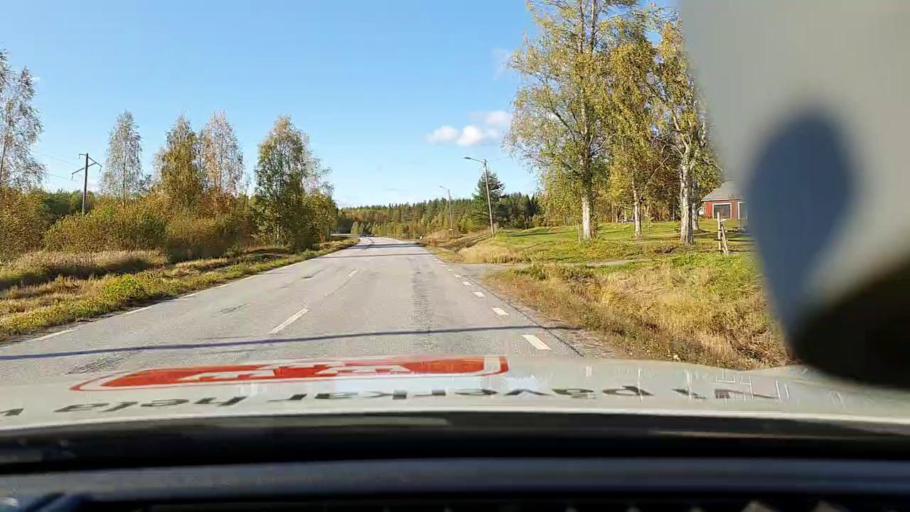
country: SE
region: Norrbotten
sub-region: Pitea Kommun
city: Norrfjarden
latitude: 65.4315
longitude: 21.4889
